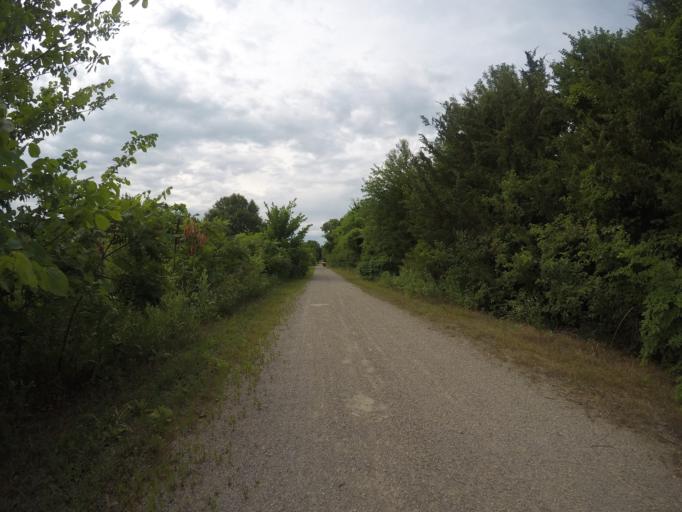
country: US
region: Kansas
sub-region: Franklin County
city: Ottawa
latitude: 38.4480
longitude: -95.2661
